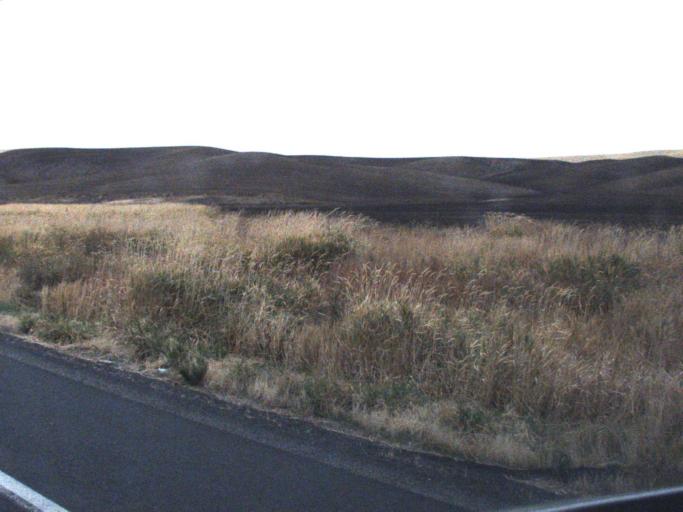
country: US
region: Washington
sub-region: Whitman County
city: Colfax
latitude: 46.9629
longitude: -117.3278
